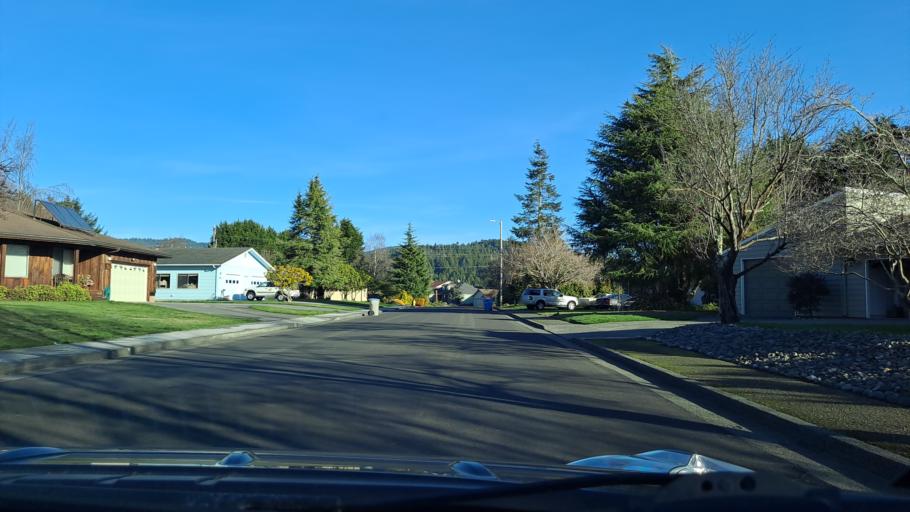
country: US
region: California
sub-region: Humboldt County
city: Fortuna
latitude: 40.5968
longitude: -124.1380
